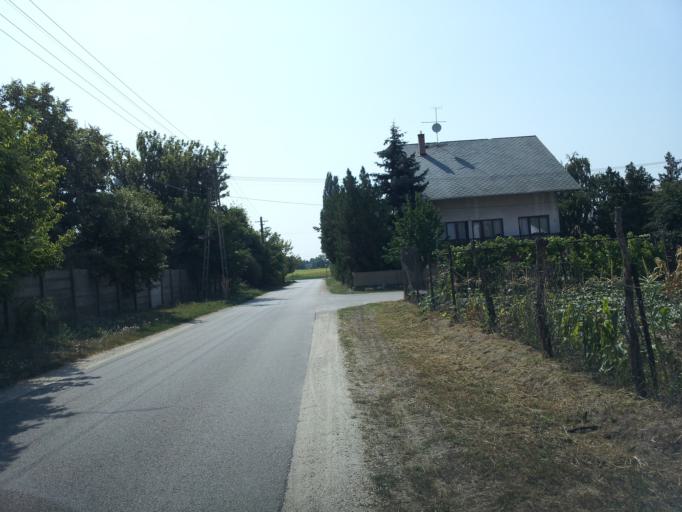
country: HU
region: Pest
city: Dunavarsany
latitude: 47.2871
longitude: 19.0366
